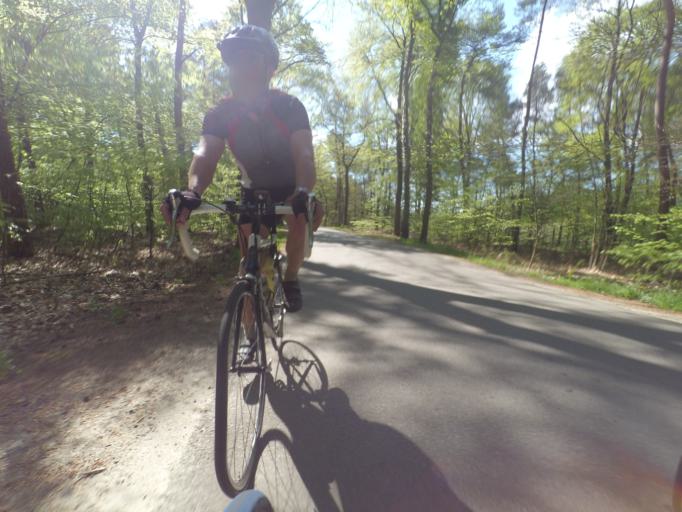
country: NL
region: Gelderland
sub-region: Gemeente Apeldoorn
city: Uddel
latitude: 52.2713
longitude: 5.7465
